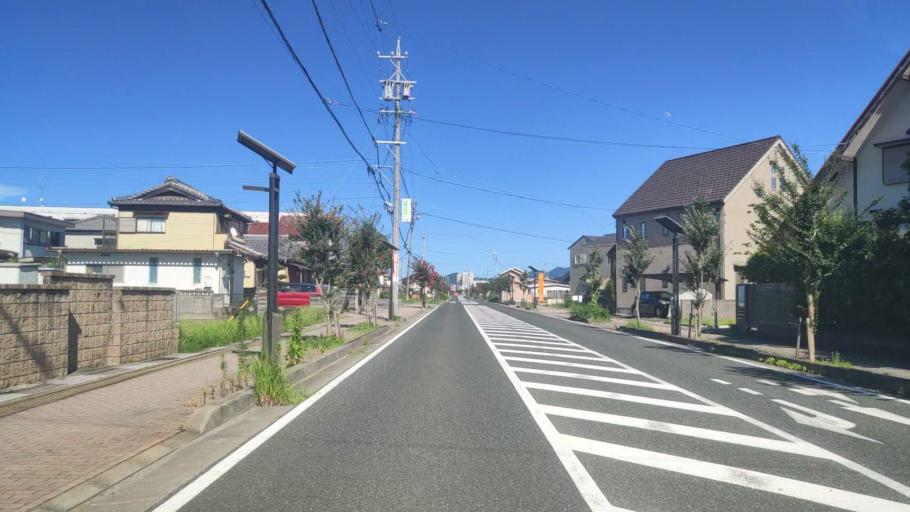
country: JP
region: Mie
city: Ise
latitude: 34.5005
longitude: 136.7029
